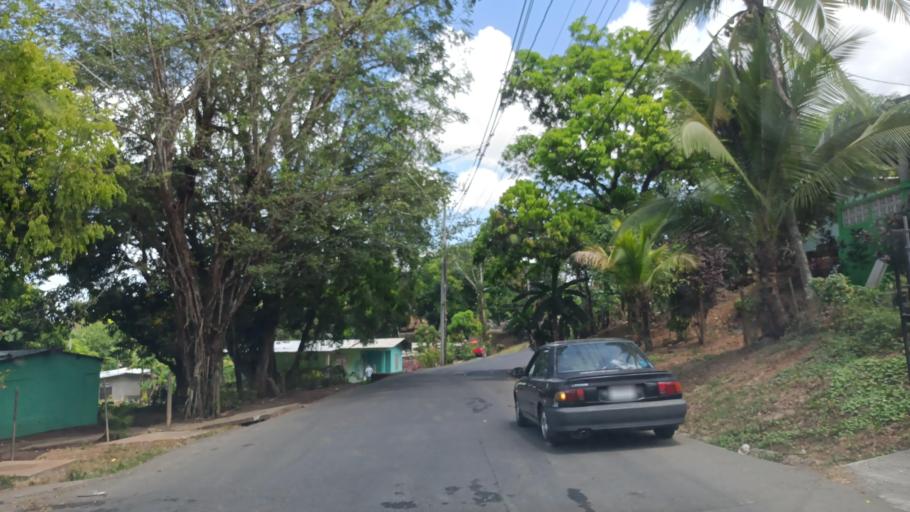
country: PA
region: Panama
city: Alcalde Diaz
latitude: 9.1002
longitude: -79.5661
